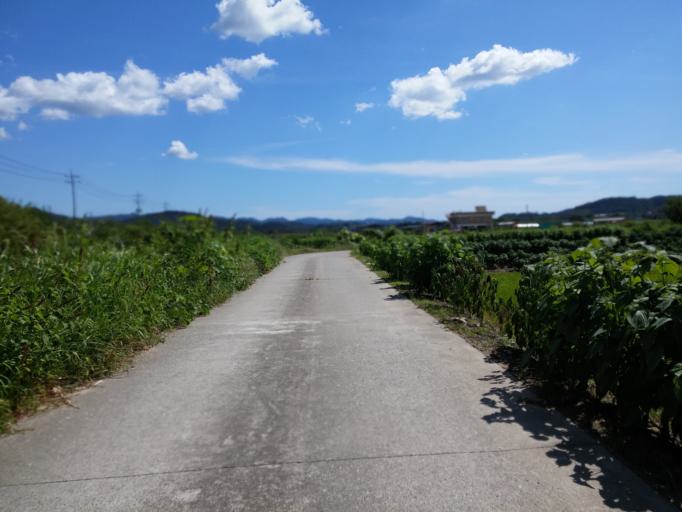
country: KR
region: Chungcheongbuk-do
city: Cheongju-si
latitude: 36.5904
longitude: 127.4971
